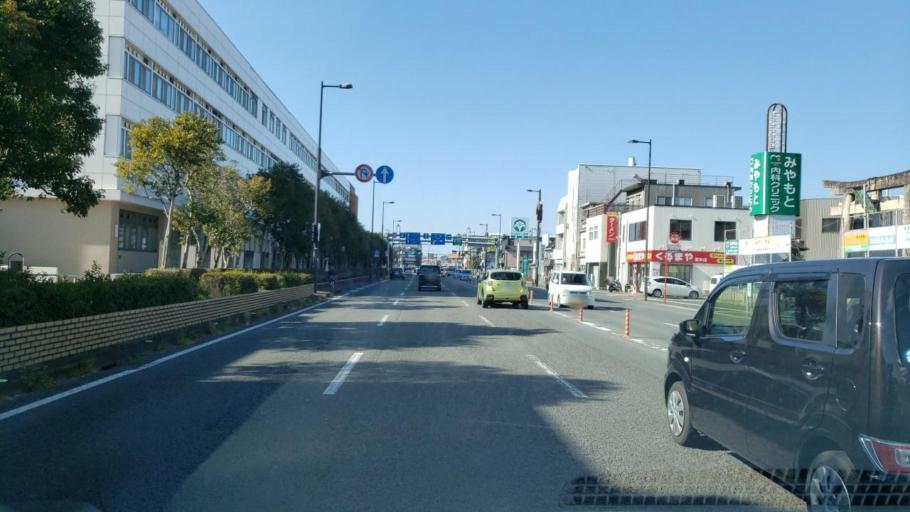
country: JP
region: Tokushima
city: Tokushima-shi
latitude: 34.0771
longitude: 134.5177
